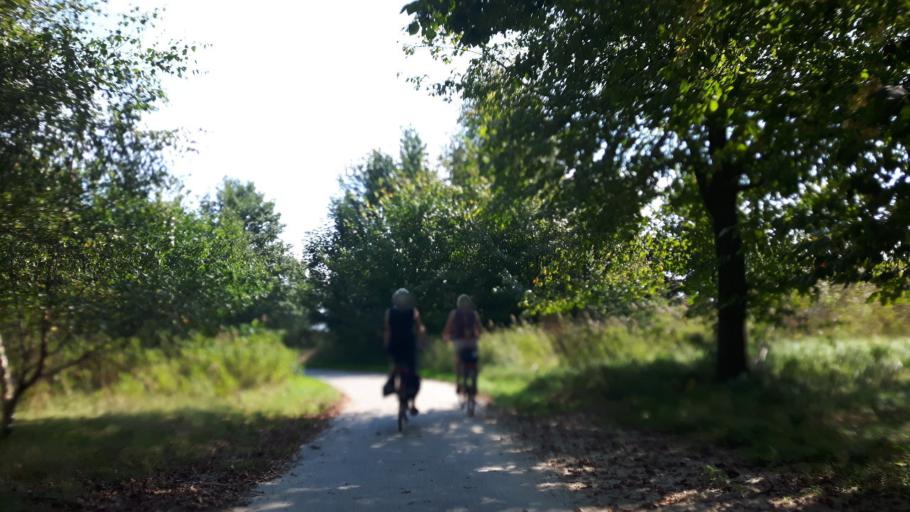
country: NL
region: Drenthe
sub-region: Gemeente Tynaarlo
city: Zuidlaren
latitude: 53.1473
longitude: 6.6956
